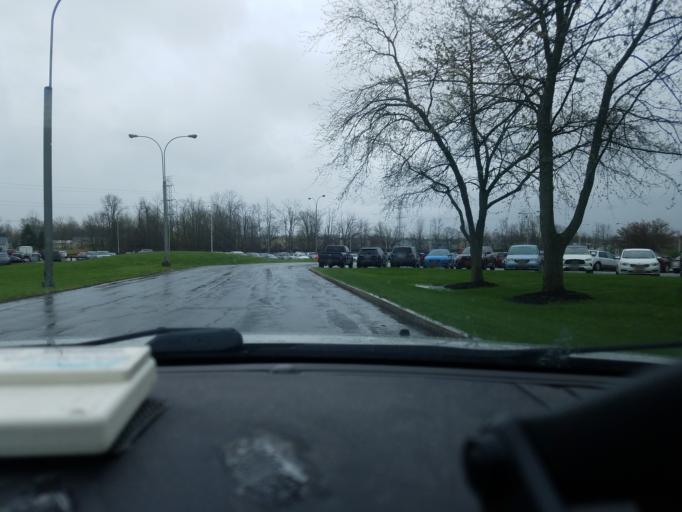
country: US
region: New York
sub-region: Onondaga County
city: North Syracuse
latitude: 43.1756
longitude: -76.1038
